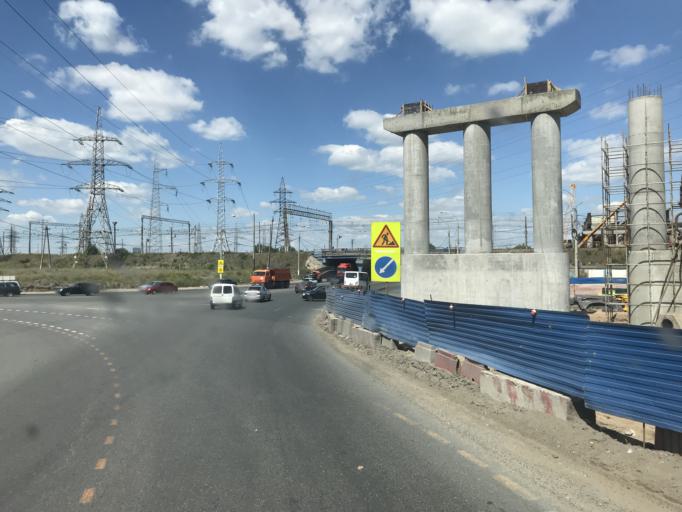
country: RU
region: Samara
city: Zhigulevsk
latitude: 53.4798
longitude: 49.5124
